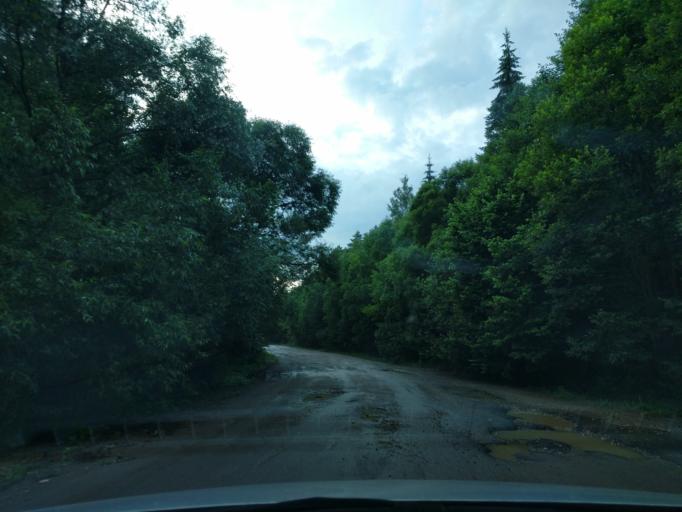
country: RU
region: Kaluga
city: Myatlevo
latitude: 54.8462
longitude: 35.6158
